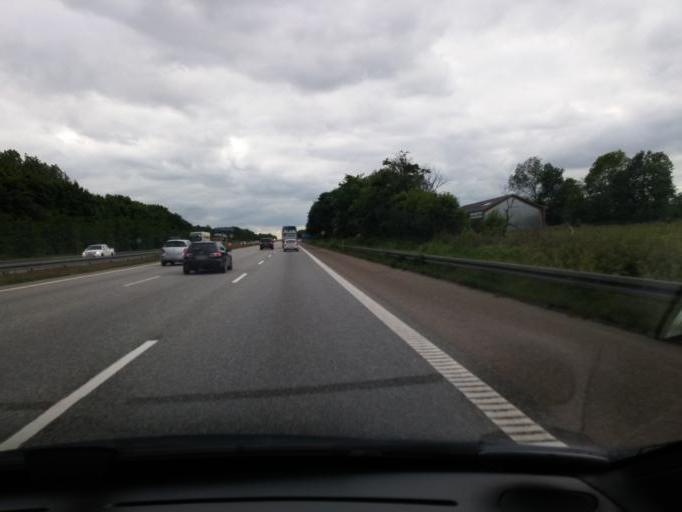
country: DK
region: Capital Region
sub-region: Brondby Kommune
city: Brondbyvester
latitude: 55.6300
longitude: 12.4074
